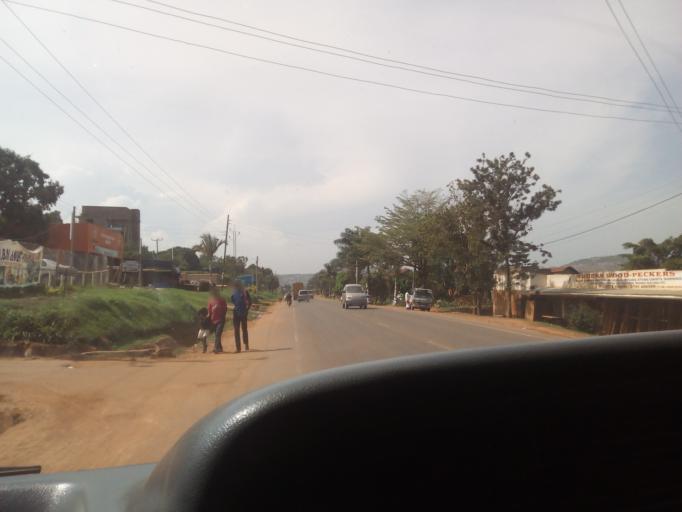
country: UG
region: Central Region
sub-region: Wakiso District
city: Kajansi
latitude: 0.2004
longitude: 32.5400
